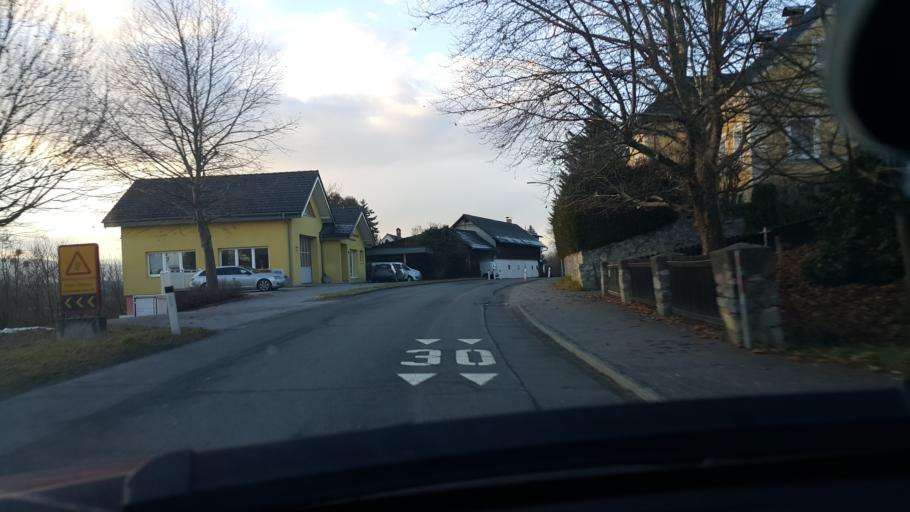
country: AT
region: Styria
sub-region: Politischer Bezirk Graz-Umgebung
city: Lieboch
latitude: 46.9657
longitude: 15.3496
